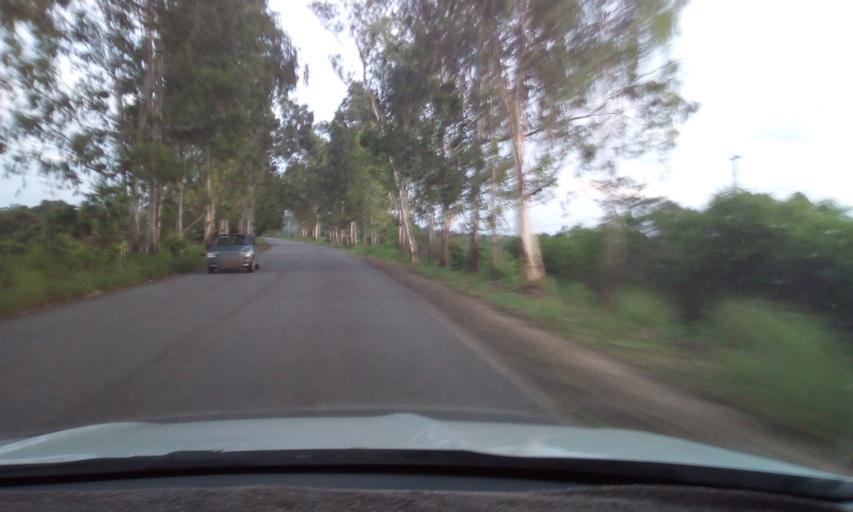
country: BR
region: Pernambuco
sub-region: Condado
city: Condado
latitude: -7.6066
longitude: -35.2085
